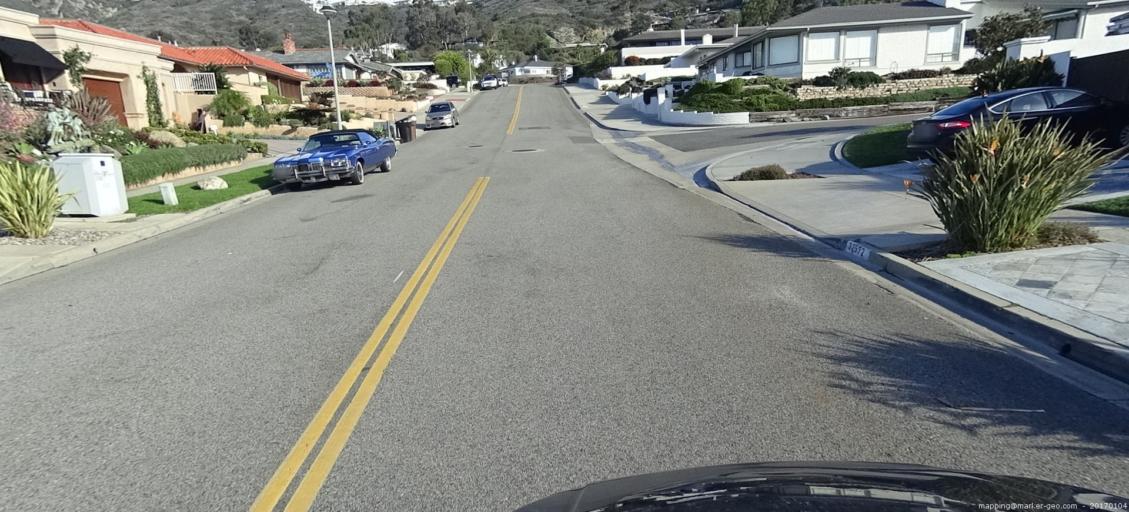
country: US
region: California
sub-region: Orange County
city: Laguna Niguel
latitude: 33.4907
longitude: -117.7294
